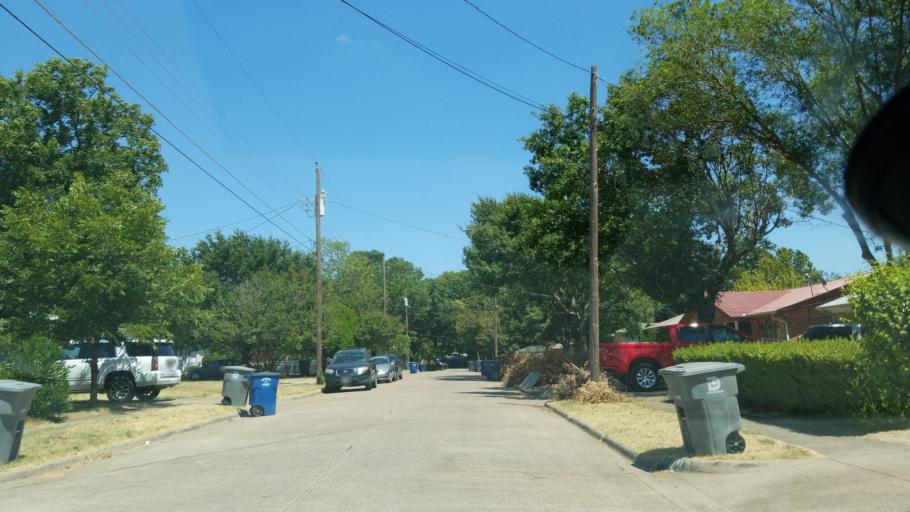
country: US
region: Texas
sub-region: Dallas County
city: Cockrell Hill
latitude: 32.7224
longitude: -96.8881
